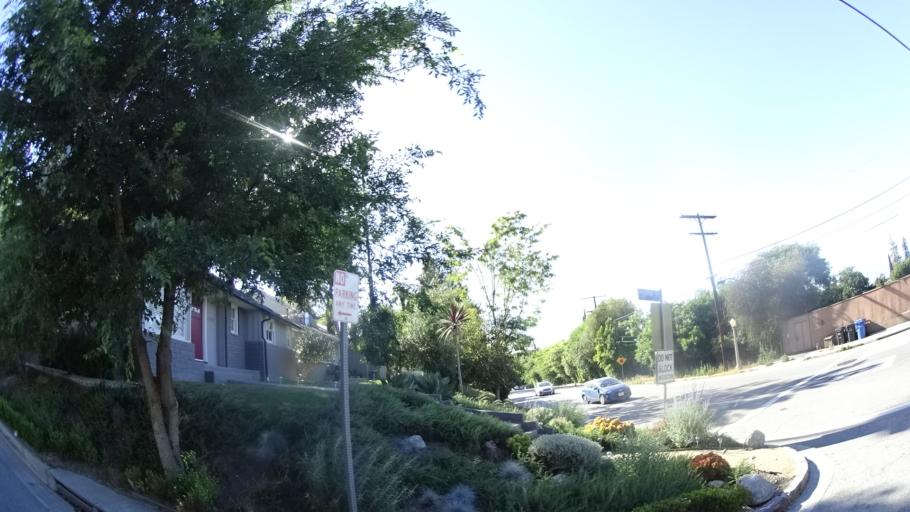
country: US
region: California
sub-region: Los Angeles County
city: Sherman Oaks
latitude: 34.1464
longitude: -118.4485
